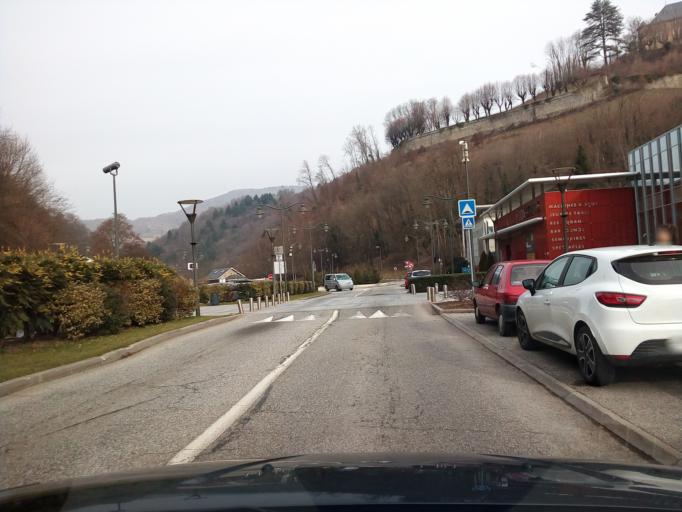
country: FR
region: Rhone-Alpes
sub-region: Departement de l'Isere
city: Vaulnaveys-le-Haut
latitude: 45.1427
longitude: 5.8294
